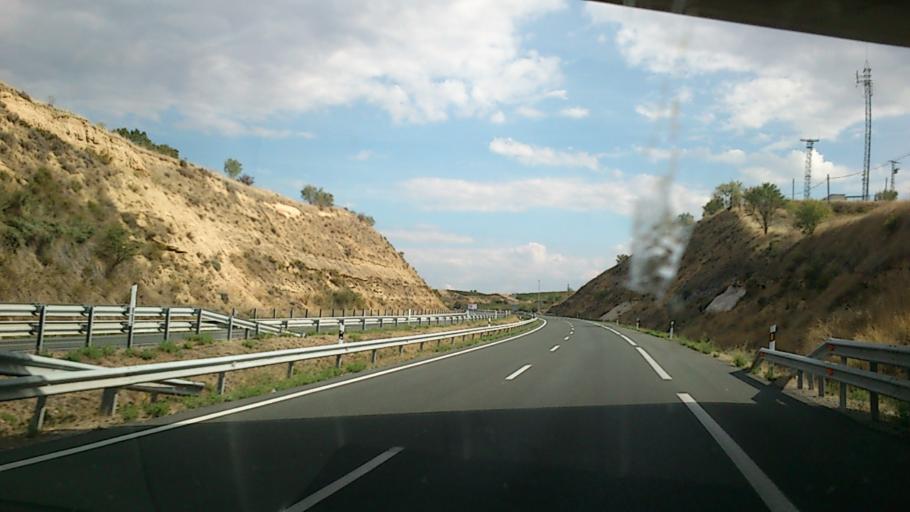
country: ES
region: La Rioja
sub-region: Provincia de La Rioja
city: Ollauri
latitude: 42.5392
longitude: -2.8389
